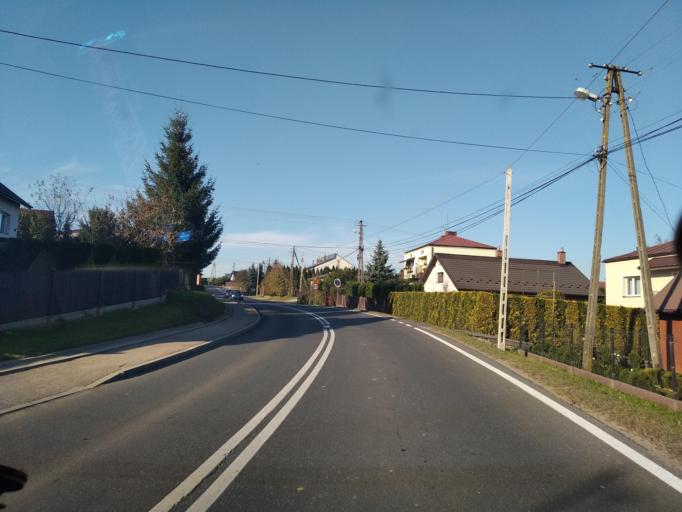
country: PL
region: Subcarpathian Voivodeship
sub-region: Powiat brzozowski
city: Humniska
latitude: 49.6808
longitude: 22.0344
